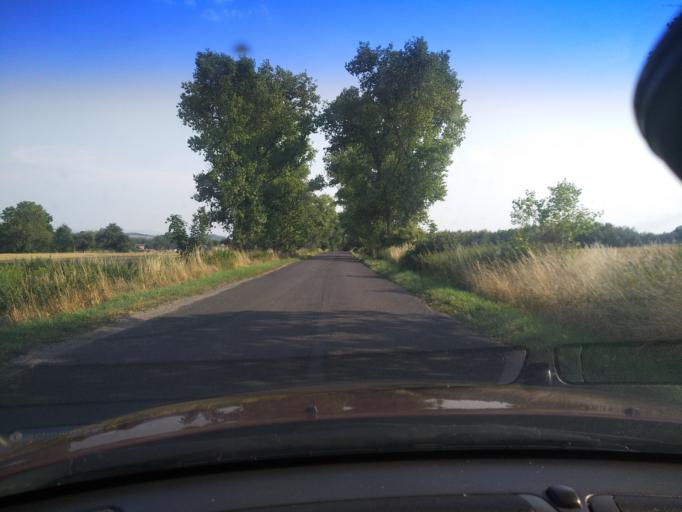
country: PL
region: Lower Silesian Voivodeship
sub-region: Powiat zgorzelecki
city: Sulikow
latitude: 51.1106
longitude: 15.0667
